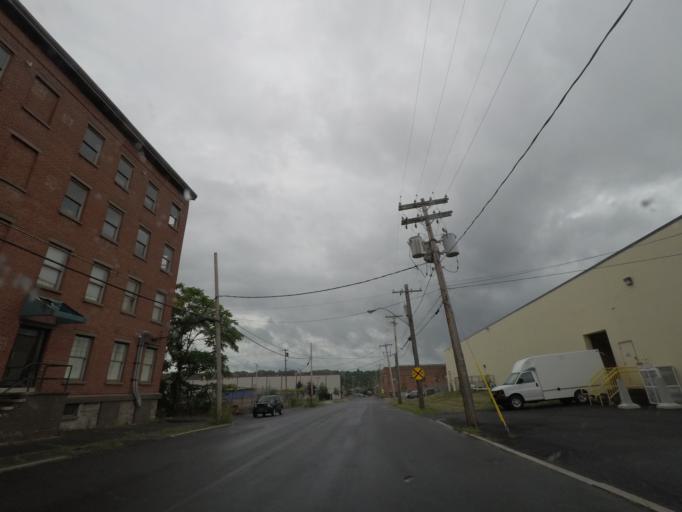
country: US
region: New York
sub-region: Albany County
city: Albany
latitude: 42.6603
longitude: -73.7450
